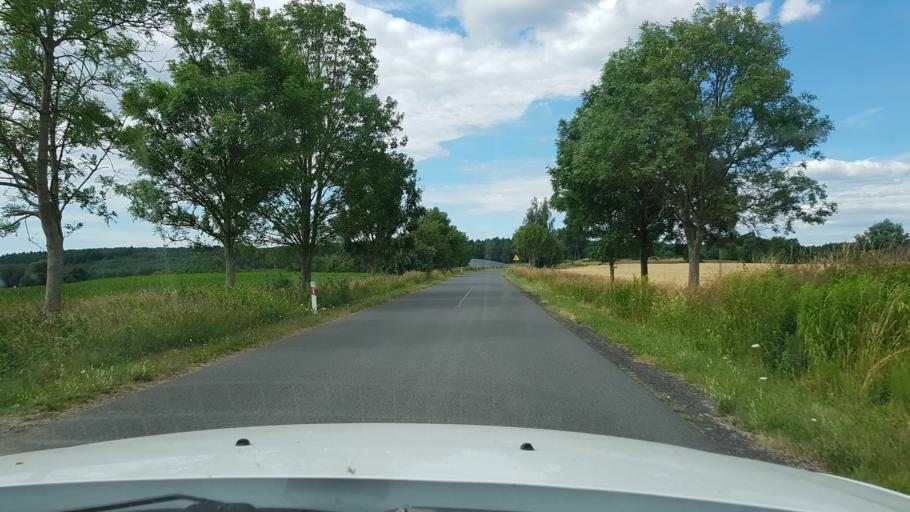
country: PL
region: West Pomeranian Voivodeship
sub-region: Powiat drawski
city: Kalisz Pomorski
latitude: 53.3486
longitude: 15.9311
